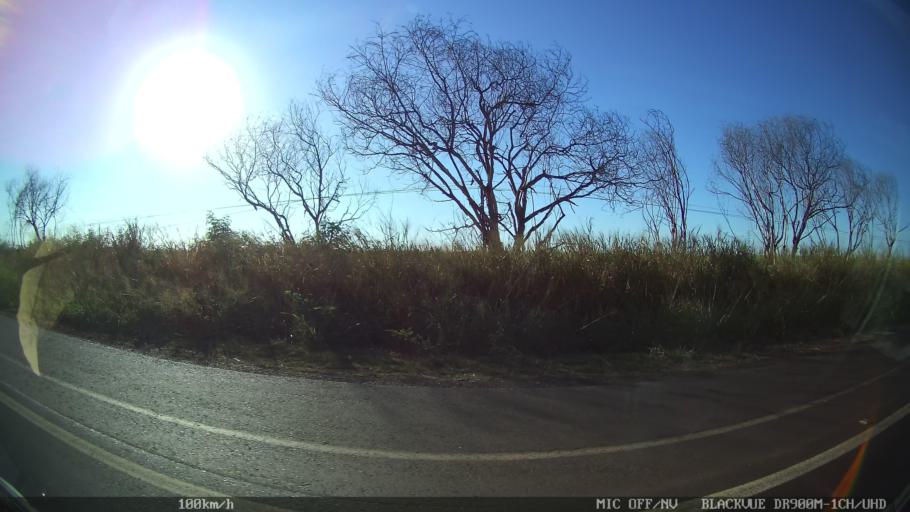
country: BR
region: Sao Paulo
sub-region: Guapiacu
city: Guapiacu
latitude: -20.7378
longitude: -49.0845
